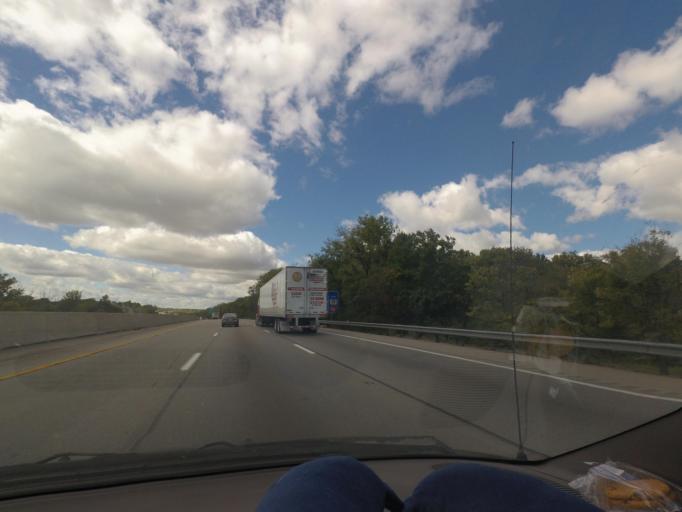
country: US
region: Ohio
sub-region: Montgomery County
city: Englewood
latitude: 39.8651
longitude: -84.2552
